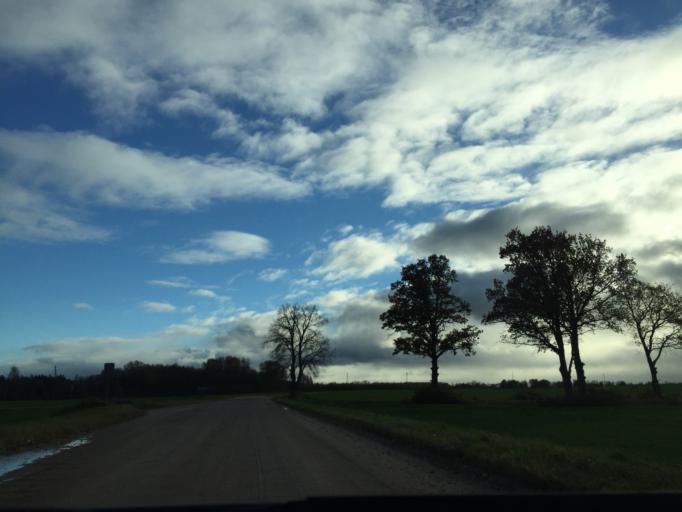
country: LV
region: Tukuma Rajons
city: Tukums
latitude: 56.9356
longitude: 22.9531
